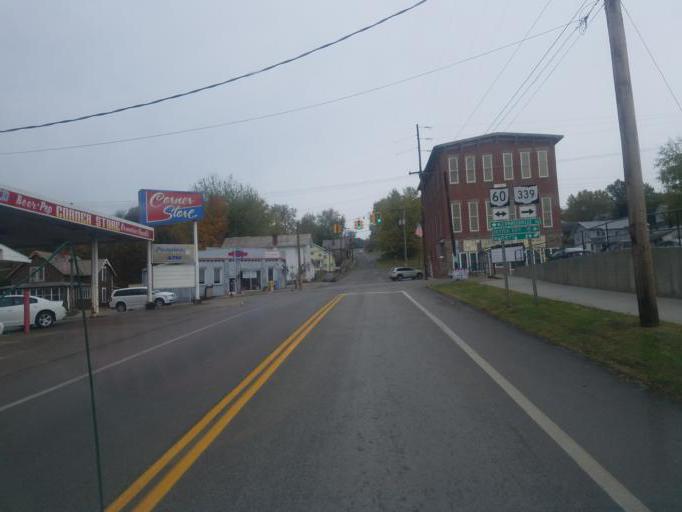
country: US
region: Ohio
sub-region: Washington County
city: Beverly
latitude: 39.5474
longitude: -81.6401
